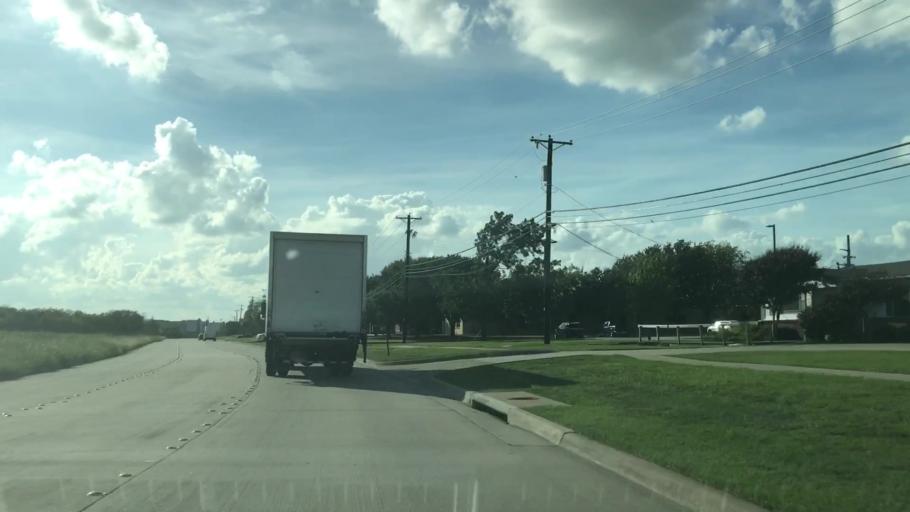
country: US
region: Texas
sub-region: Dallas County
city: Coppell
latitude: 32.9481
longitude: -96.9959
